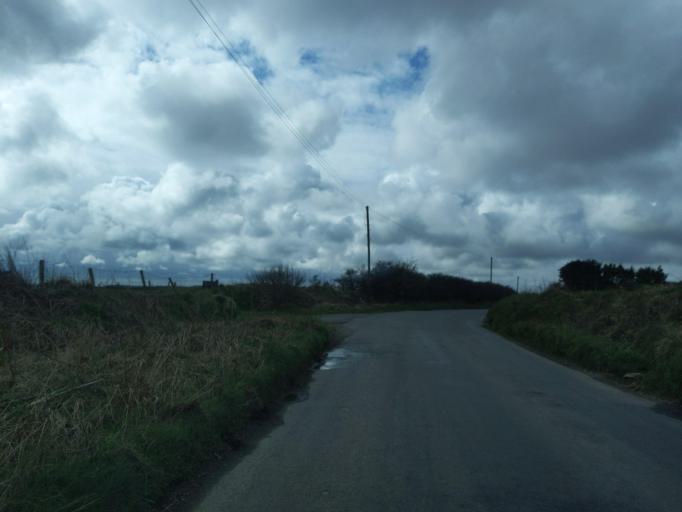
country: GB
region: England
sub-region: Cornwall
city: Camelford
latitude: 50.6408
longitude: -4.6473
